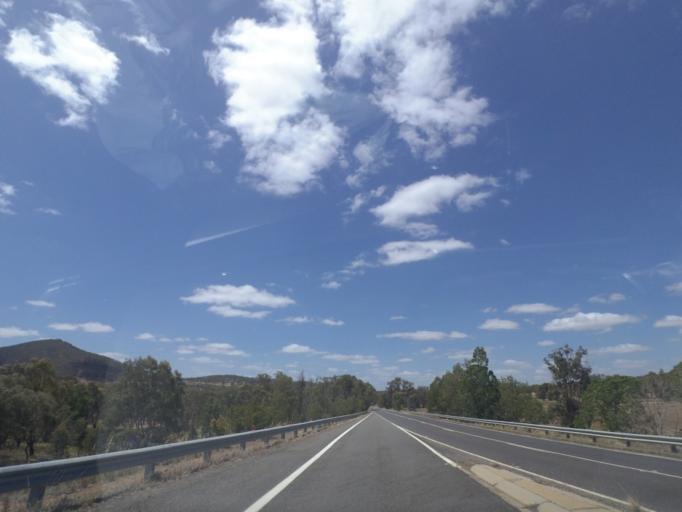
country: AU
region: Victoria
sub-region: Wangaratta
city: Wangaratta
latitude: -36.4663
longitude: 146.2116
